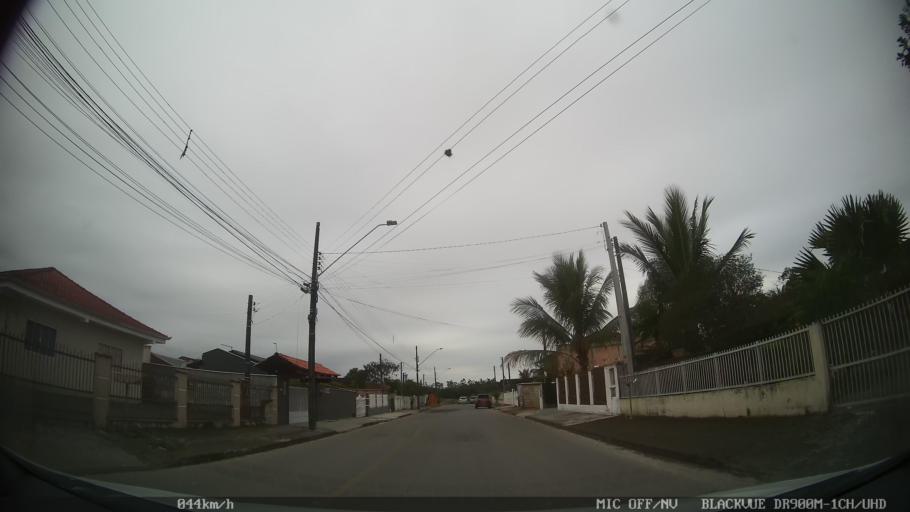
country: BR
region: Santa Catarina
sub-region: Joinville
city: Joinville
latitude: -26.2962
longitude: -48.9095
